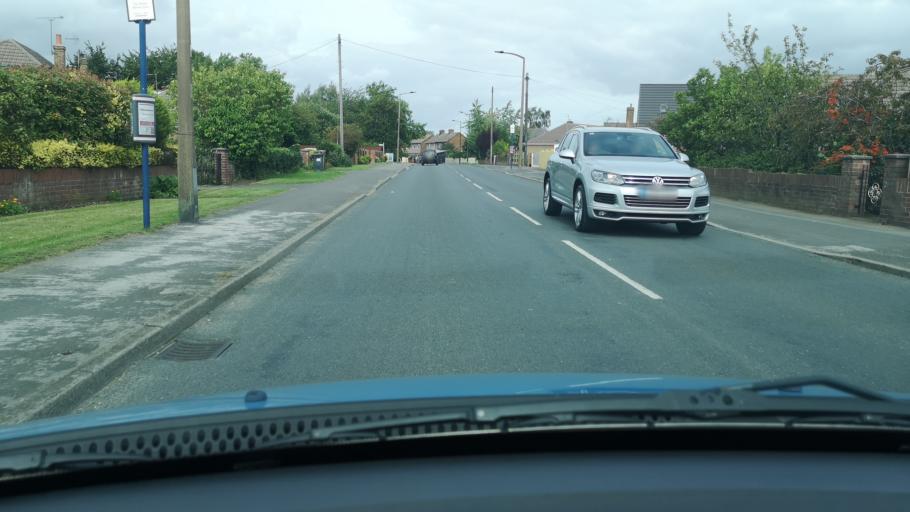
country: GB
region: England
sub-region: Doncaster
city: Kirk Sandall
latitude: 53.5749
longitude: -1.0671
